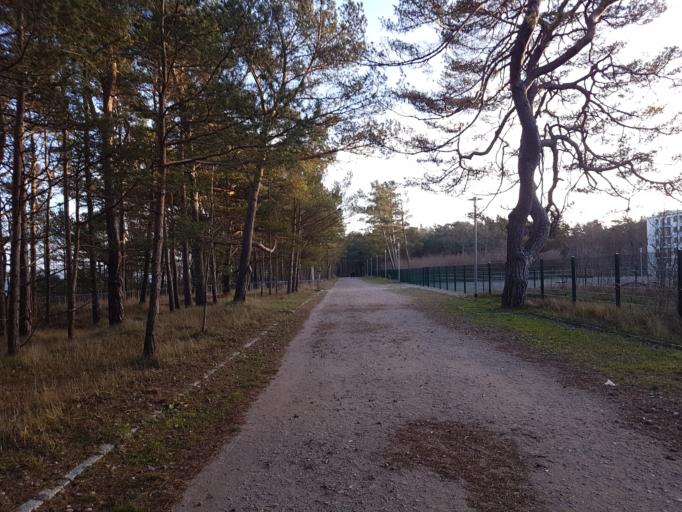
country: DE
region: Mecklenburg-Vorpommern
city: Ostseebad Binz
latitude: 54.4284
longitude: 13.5843
